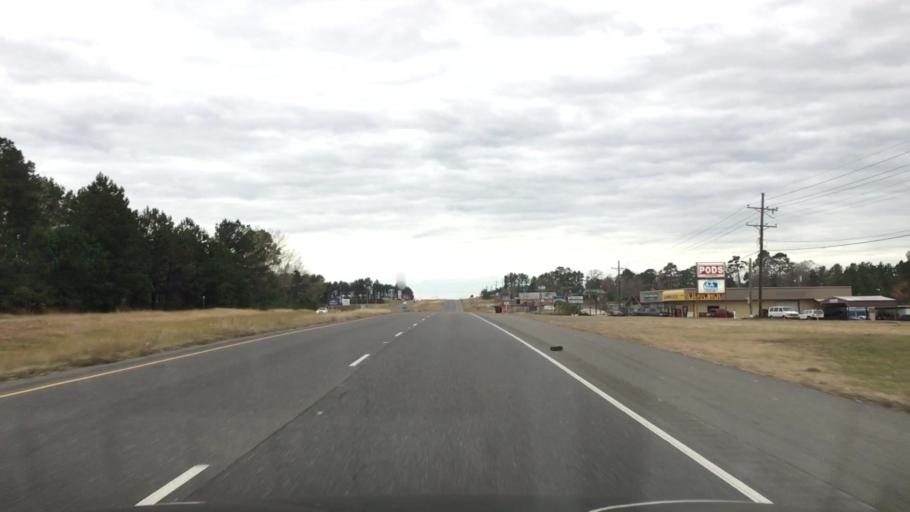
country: US
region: Louisiana
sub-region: Vernon Parish
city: New Llano
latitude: 31.0955
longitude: -93.2700
